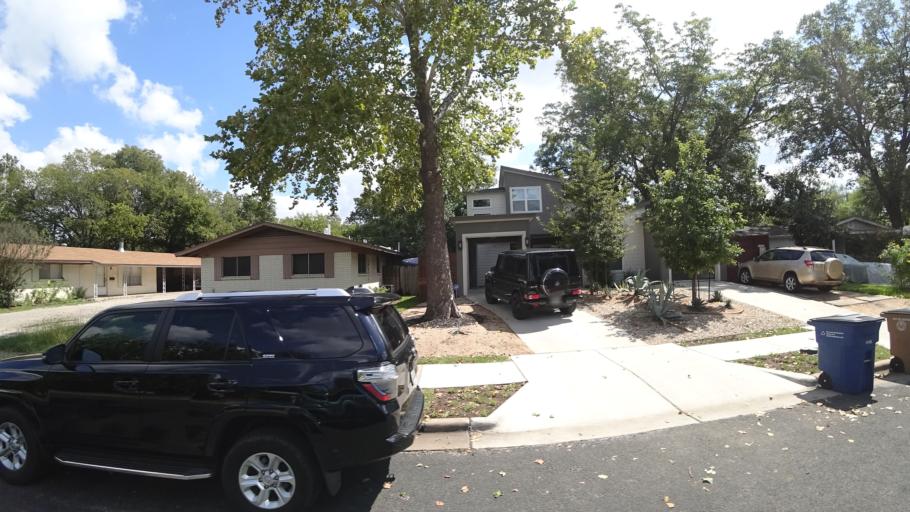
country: US
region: Texas
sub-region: Williamson County
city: Jollyville
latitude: 30.3630
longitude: -97.7270
